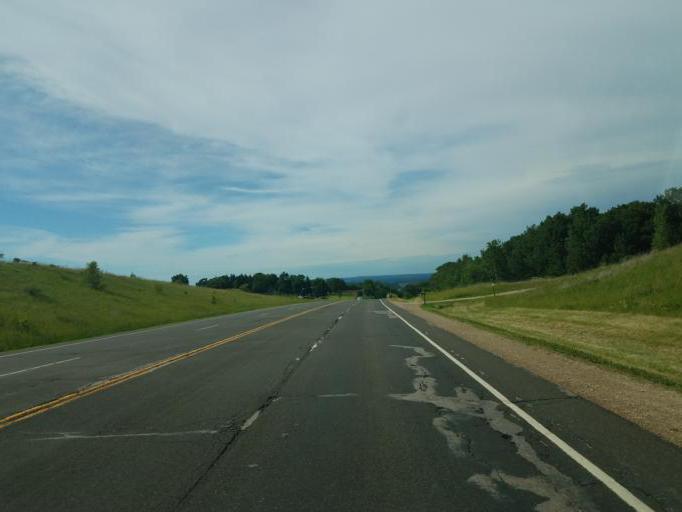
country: US
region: Wisconsin
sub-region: Monroe County
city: Tomah
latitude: 43.9003
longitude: -90.4910
